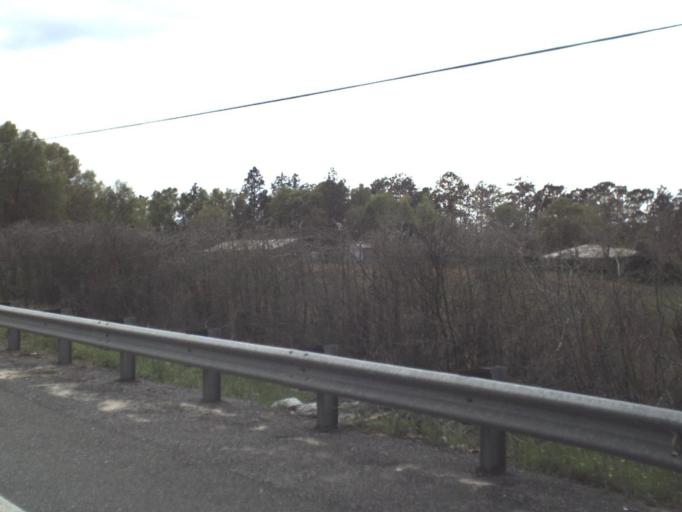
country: US
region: Florida
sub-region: Okaloosa County
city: Crestview
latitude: 30.8391
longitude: -86.5305
